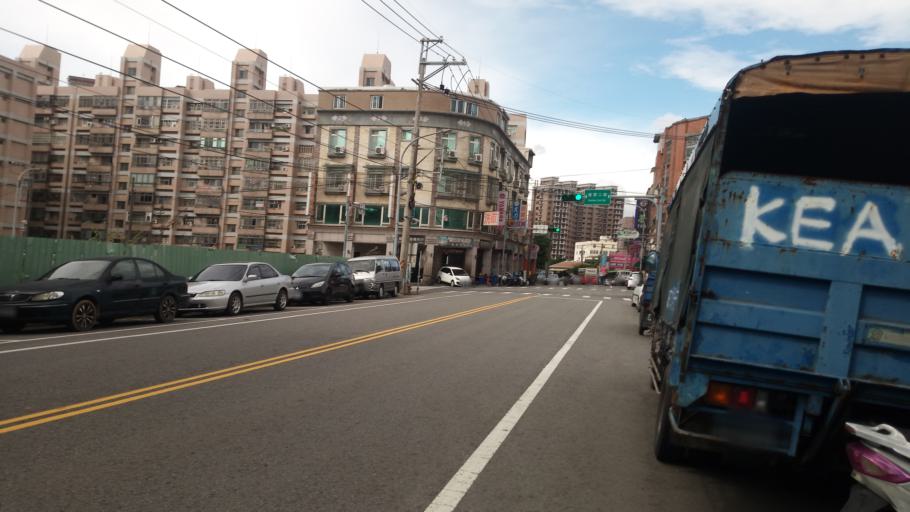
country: TW
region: Taiwan
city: Daxi
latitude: 24.9381
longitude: 121.2465
